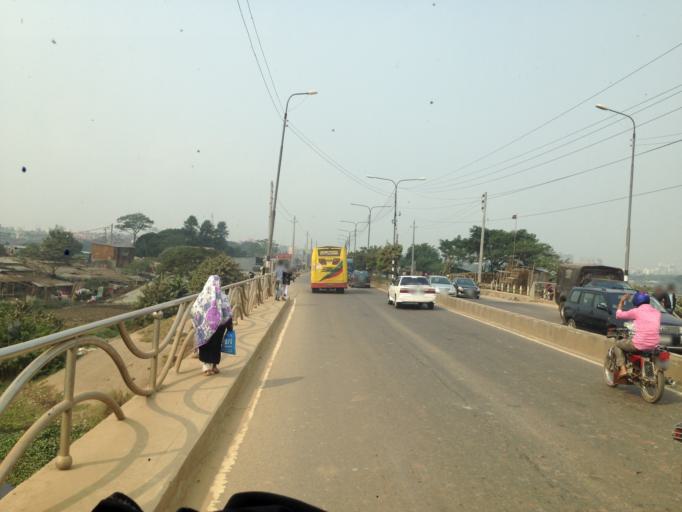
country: BD
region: Dhaka
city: Tungi
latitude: 23.8211
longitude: 90.3839
